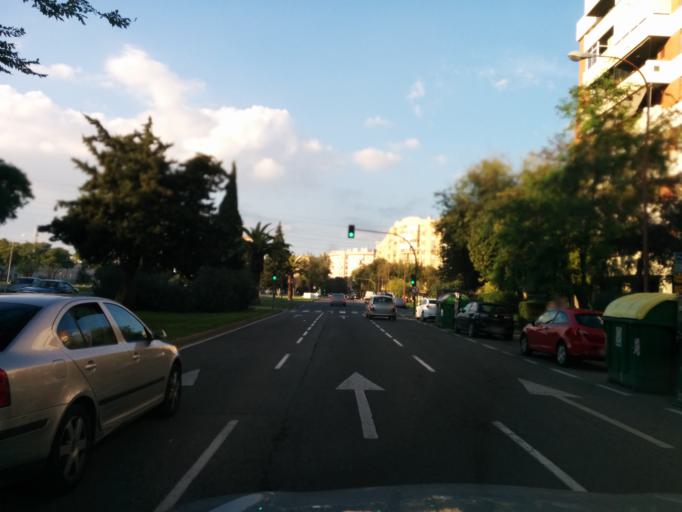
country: ES
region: Andalusia
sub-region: Provincia de Sevilla
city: Sevilla
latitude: 37.3891
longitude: -5.9200
